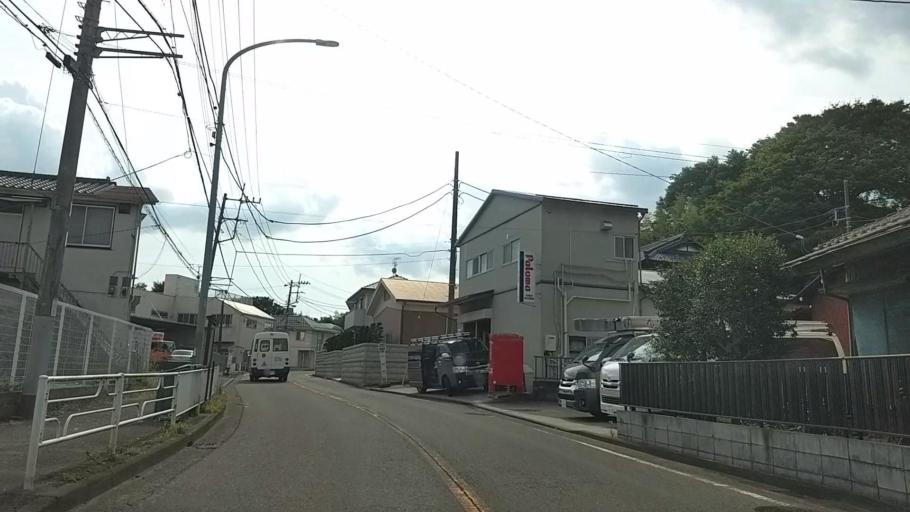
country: JP
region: Kanagawa
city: Yokohama
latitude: 35.4908
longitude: 139.5823
